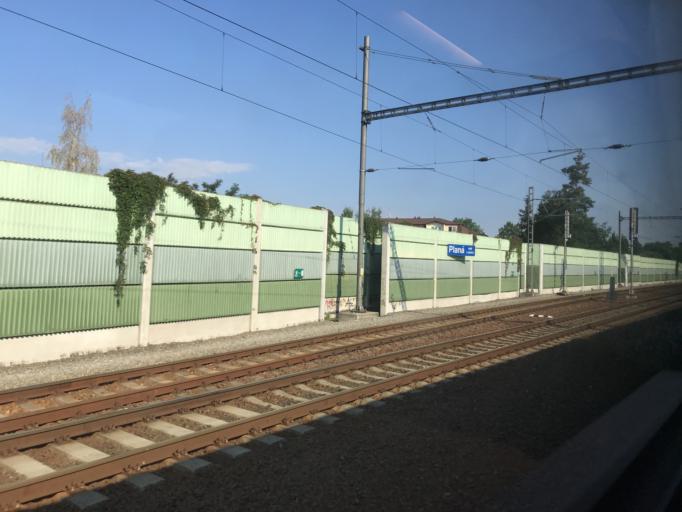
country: CZ
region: Jihocesky
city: Plana nad Luznici
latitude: 49.3503
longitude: 14.7078
